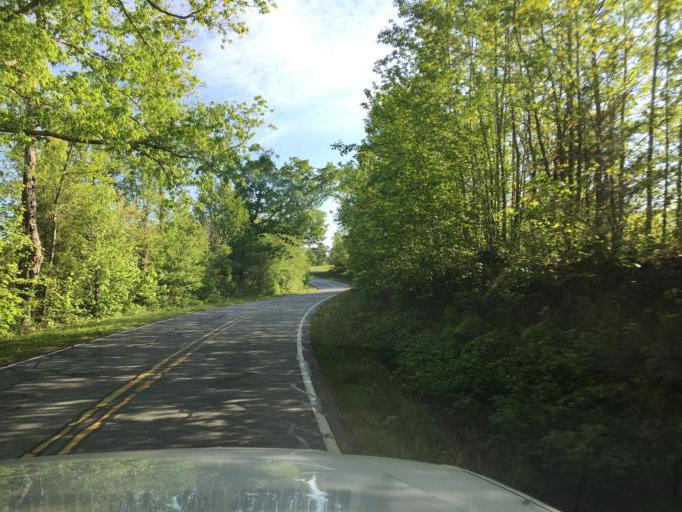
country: US
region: North Carolina
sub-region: Rutherford County
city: Rutherfordton
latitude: 35.3240
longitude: -81.9903
